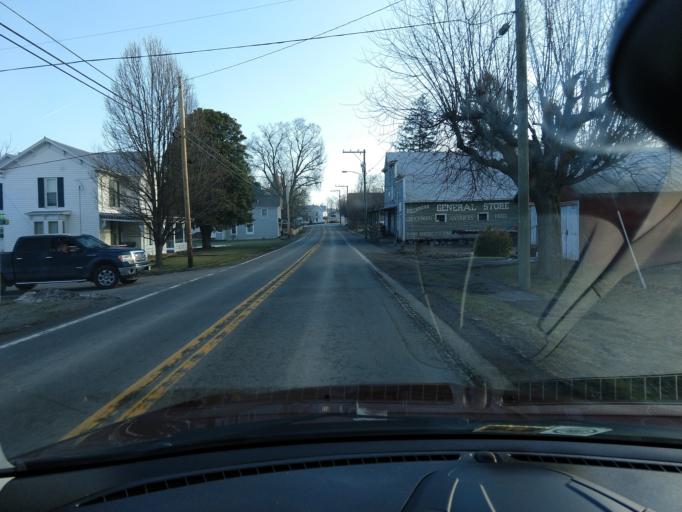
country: US
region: West Virginia
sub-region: Pocahontas County
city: Marlinton
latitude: 38.1342
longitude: -80.2142
